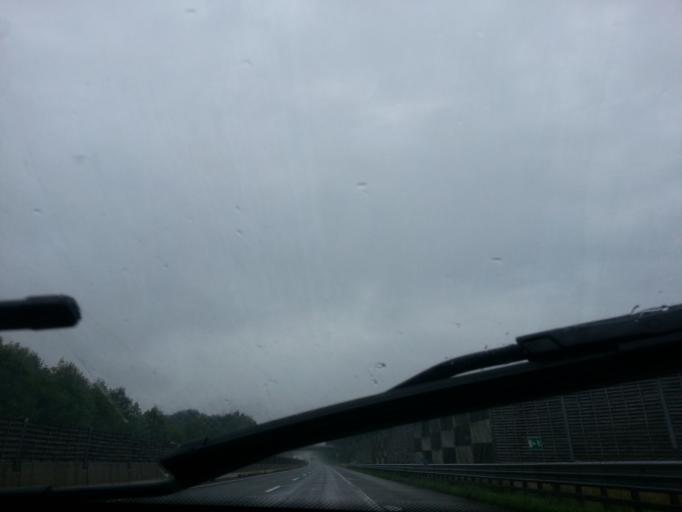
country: AT
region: Upper Austria
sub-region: Politischer Bezirk Vocklabruck
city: Gampern
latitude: 47.9557
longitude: 13.5473
